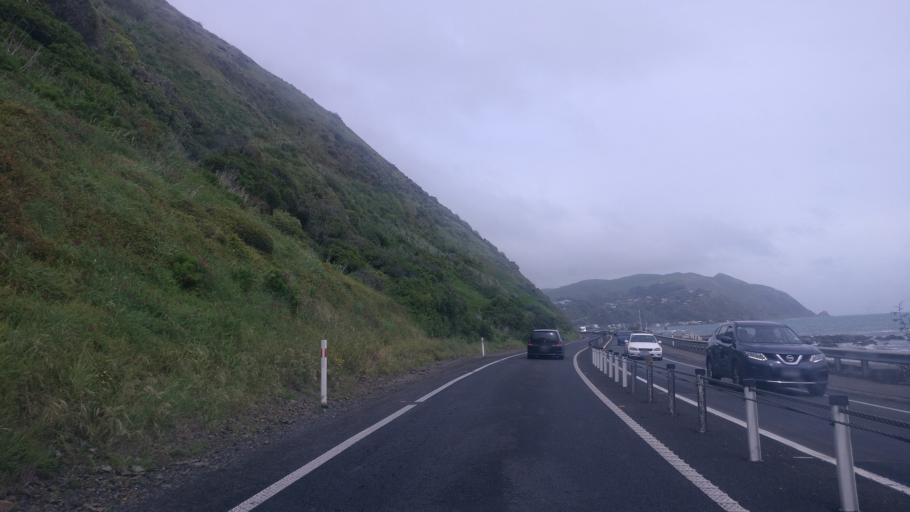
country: NZ
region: Wellington
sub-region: Porirua City
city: Porirua
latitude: -41.0218
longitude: 174.9093
